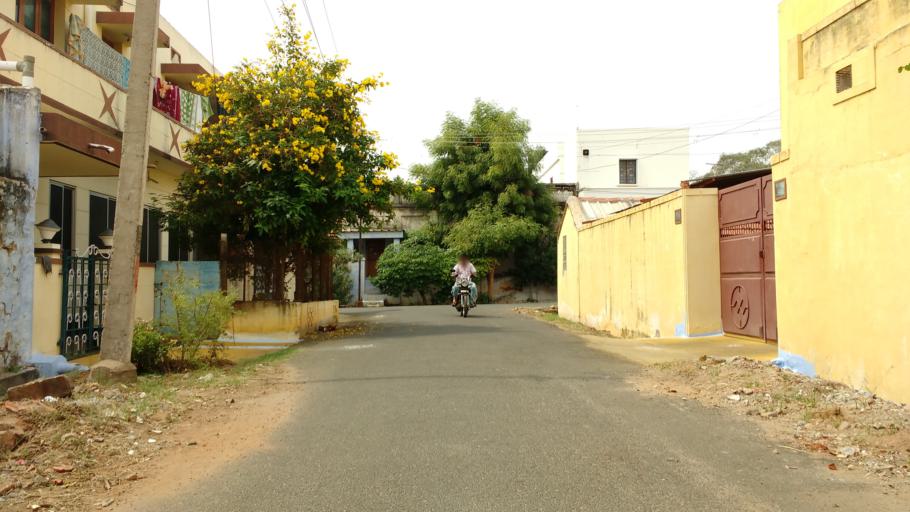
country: IN
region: Tamil Nadu
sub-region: Erode
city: Gobichettipalayam
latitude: 11.4578
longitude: 77.4315
